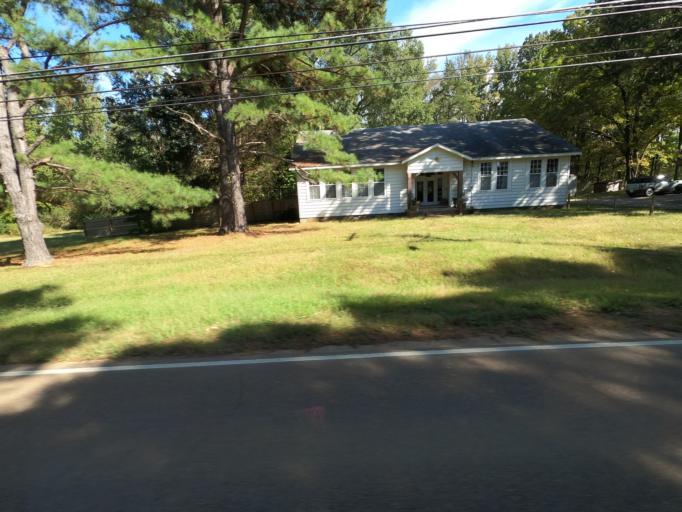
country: US
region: Tennessee
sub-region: Shelby County
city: Arlington
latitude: 35.2388
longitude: -89.6500
